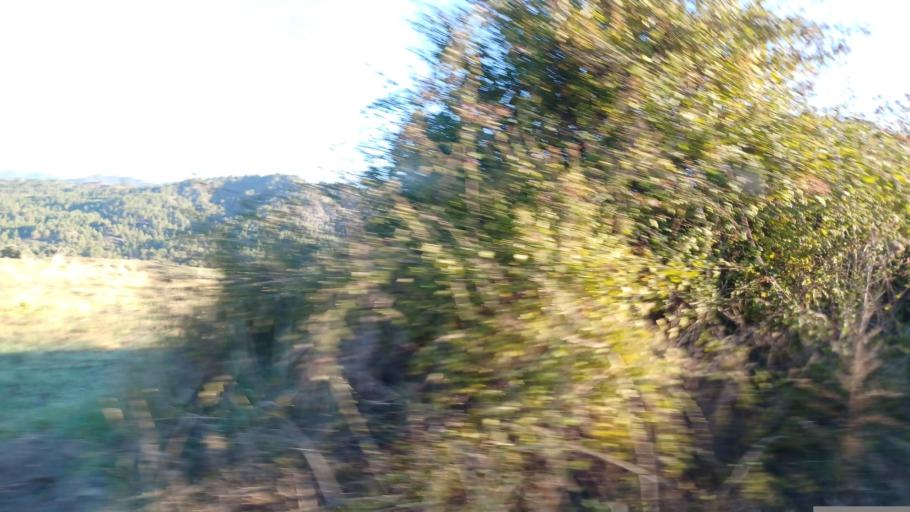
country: CY
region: Pafos
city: Polis
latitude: 34.9495
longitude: 32.5536
